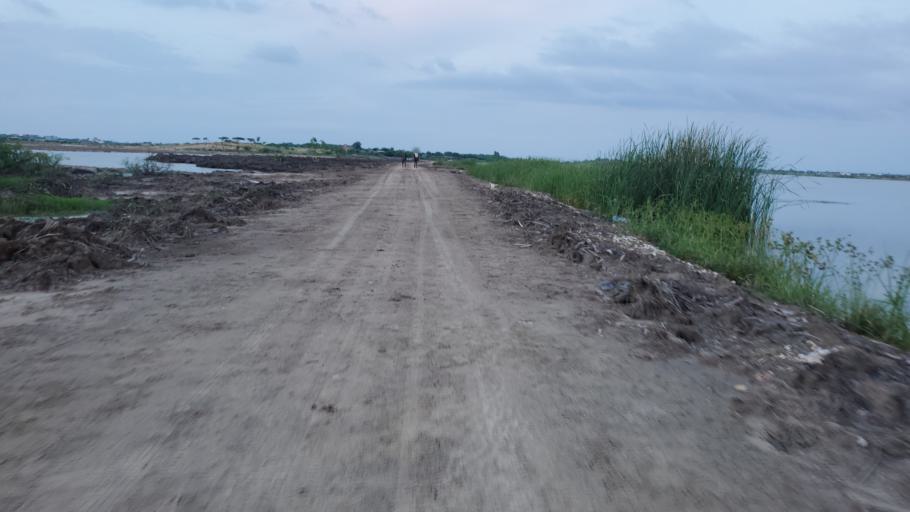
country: SN
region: Saint-Louis
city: Saint-Louis
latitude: 16.0433
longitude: -16.4163
